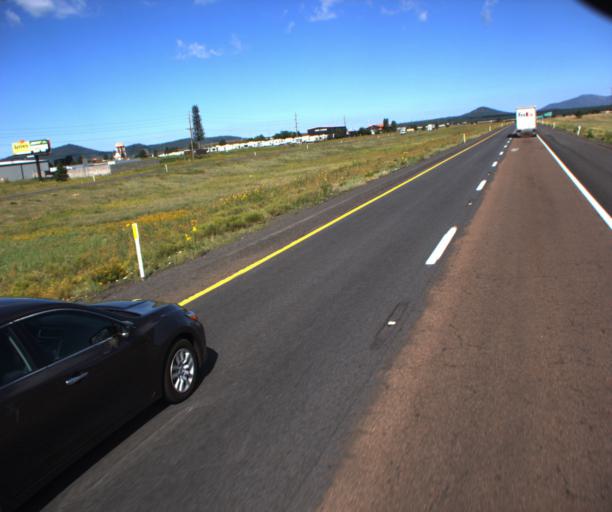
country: US
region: Arizona
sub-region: Coconino County
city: Parks
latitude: 35.2314
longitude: -111.8117
